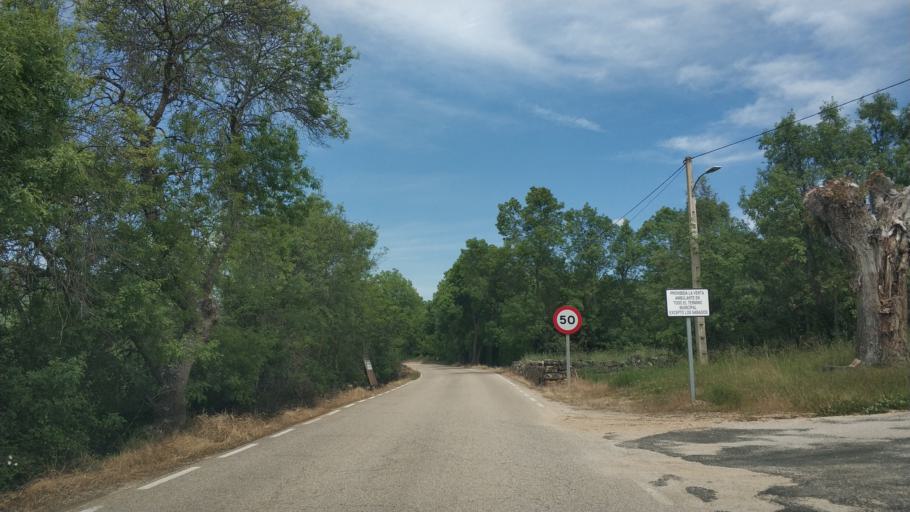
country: ES
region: Castille and Leon
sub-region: Provincia de Soria
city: Sotillo del Rincon
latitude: 41.9016
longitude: -2.6404
